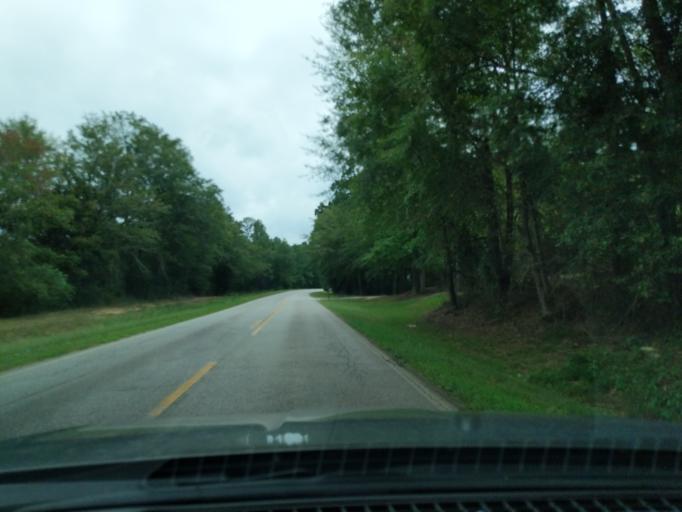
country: US
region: Georgia
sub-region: Columbia County
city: Appling
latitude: 33.5887
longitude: -82.3785
